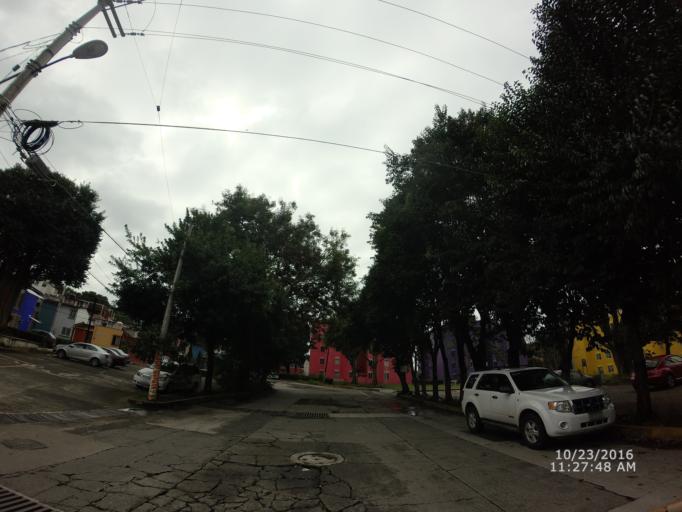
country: MX
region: Veracruz
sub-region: Tlalnelhuayocan
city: Guadalupe Victoria
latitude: 19.5473
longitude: -96.9406
